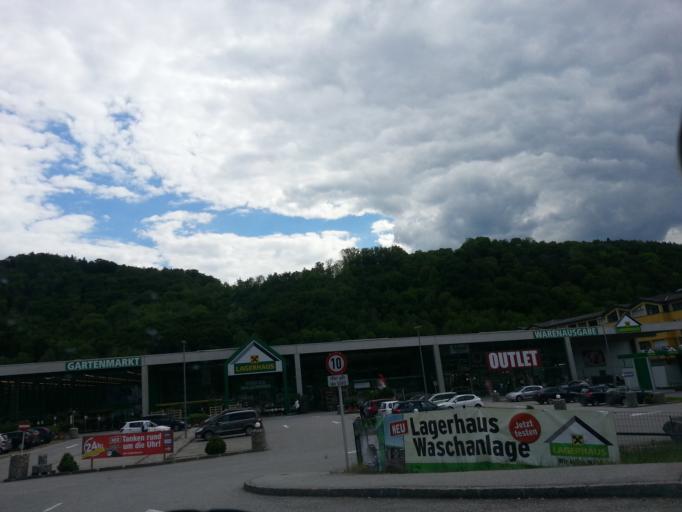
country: AT
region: Salzburg
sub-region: Politischer Bezirk Salzburg-Umgebung
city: Bergheim
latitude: 47.8430
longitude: 13.0424
